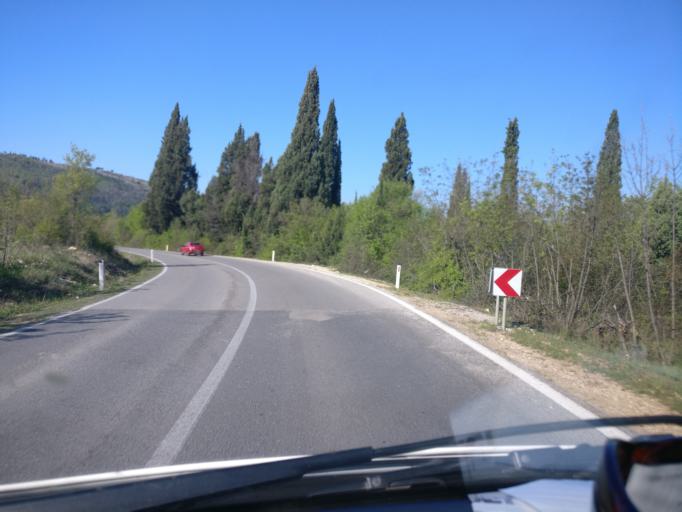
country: BA
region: Federation of Bosnia and Herzegovina
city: Tasovcici
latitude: 43.1232
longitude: 17.7498
